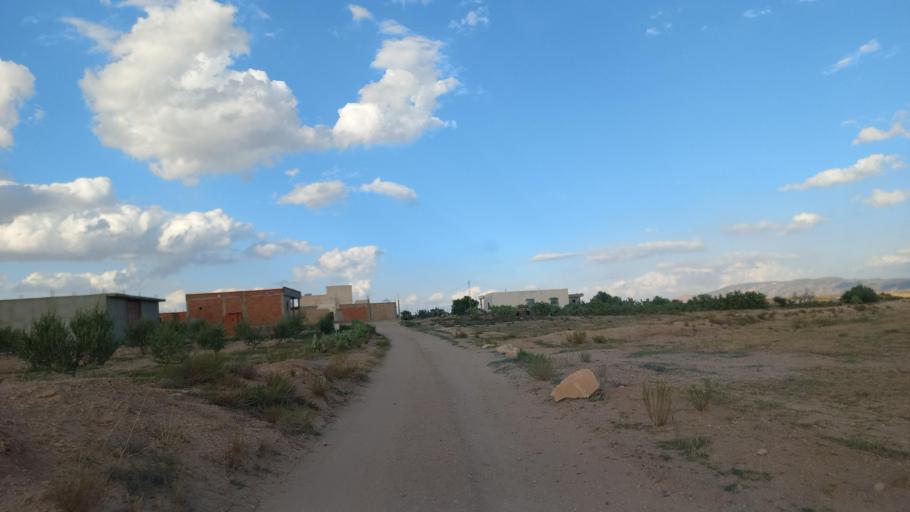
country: TN
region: Al Qasrayn
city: Sbiba
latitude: 35.3846
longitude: 9.0459
